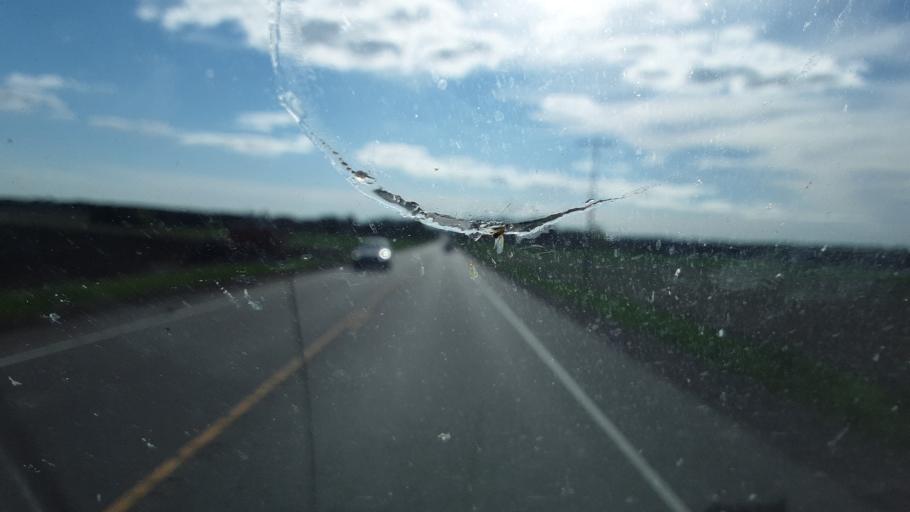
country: US
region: Wisconsin
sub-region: Wood County
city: Marshfield
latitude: 44.6556
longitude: -90.2015
